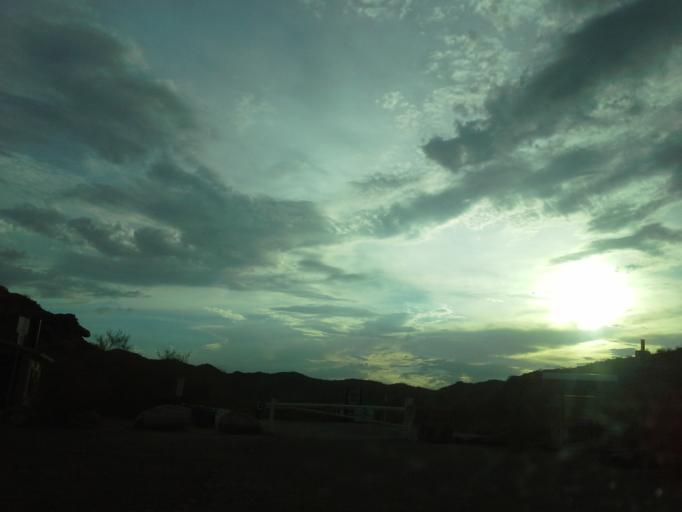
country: US
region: Arizona
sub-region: Maricopa County
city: Guadalupe
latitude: 33.3629
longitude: -111.9857
